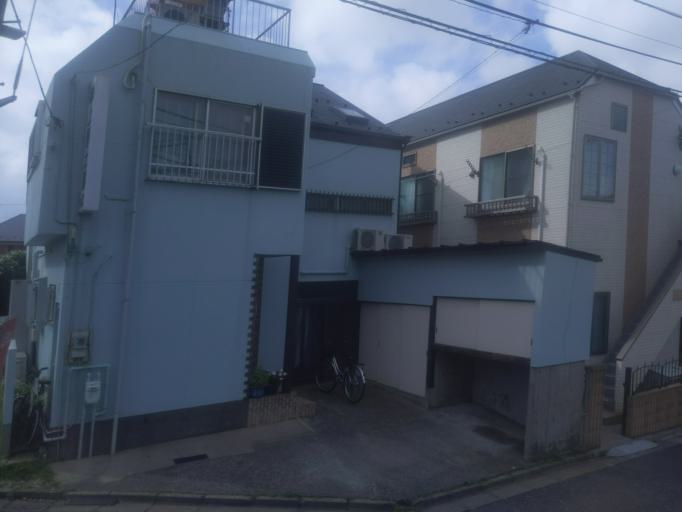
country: JP
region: Saitama
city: Wako
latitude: 35.7229
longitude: 139.6316
